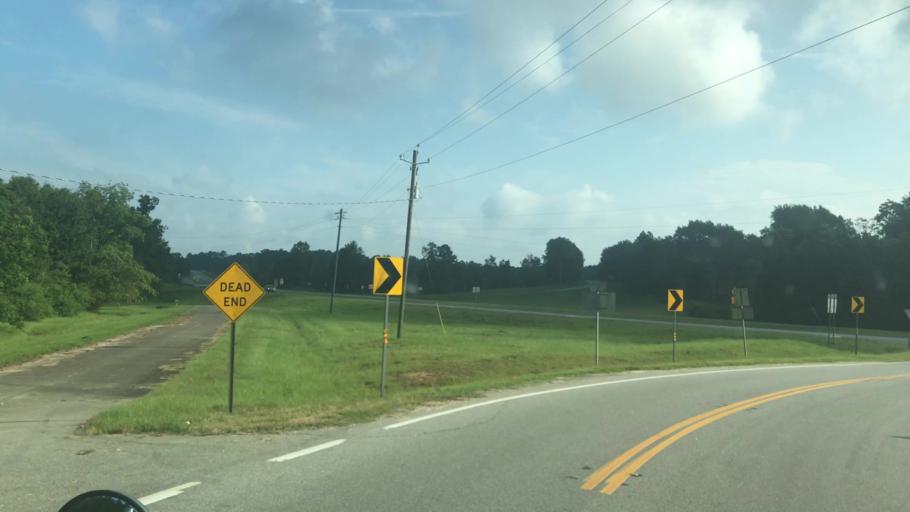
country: US
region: Georgia
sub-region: Decatur County
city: Bainbridge
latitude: 30.7755
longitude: -84.4887
